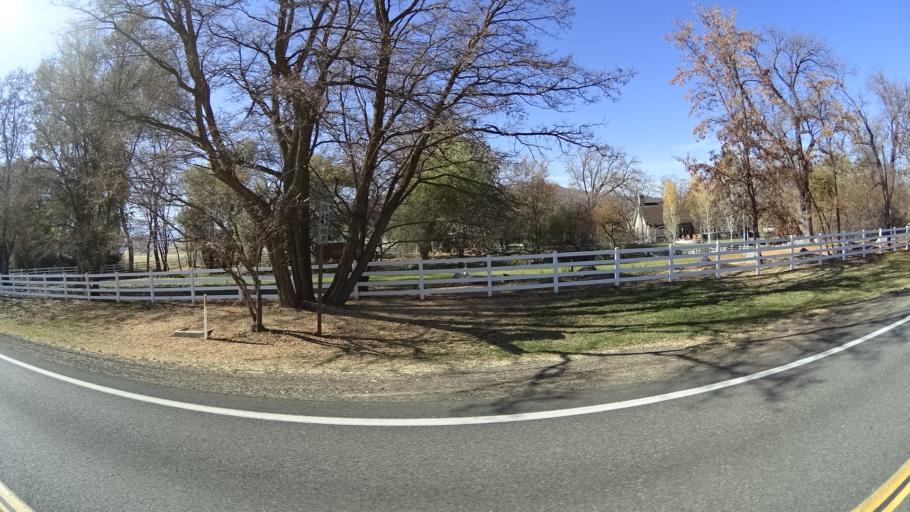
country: US
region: California
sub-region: Siskiyou County
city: Weed
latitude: 41.5173
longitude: -122.5190
